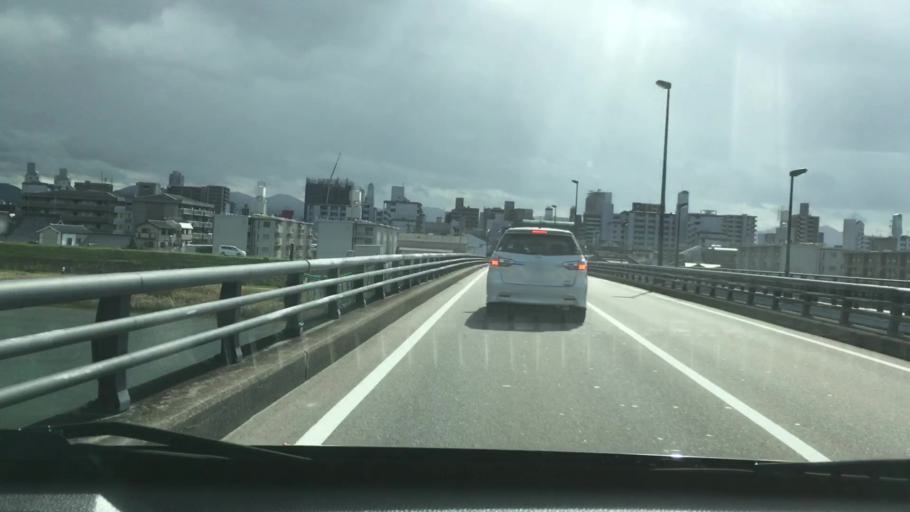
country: JP
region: Hiroshima
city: Hiroshima-shi
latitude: 34.3989
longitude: 132.4326
